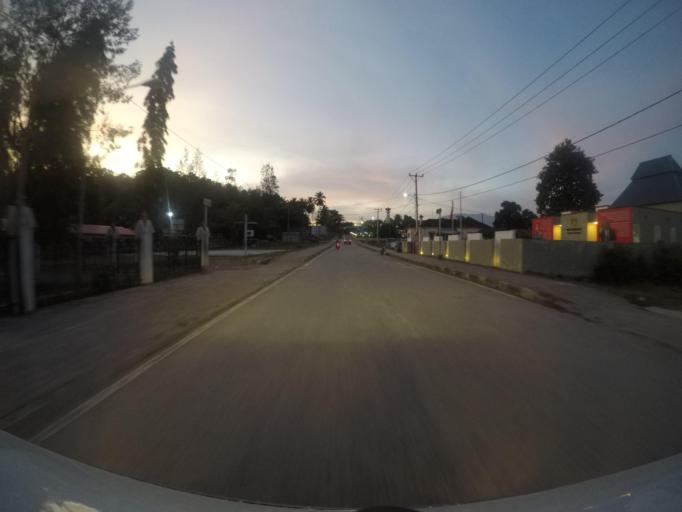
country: TL
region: Viqueque
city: Viqueque
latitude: -8.8685
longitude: 126.3656
